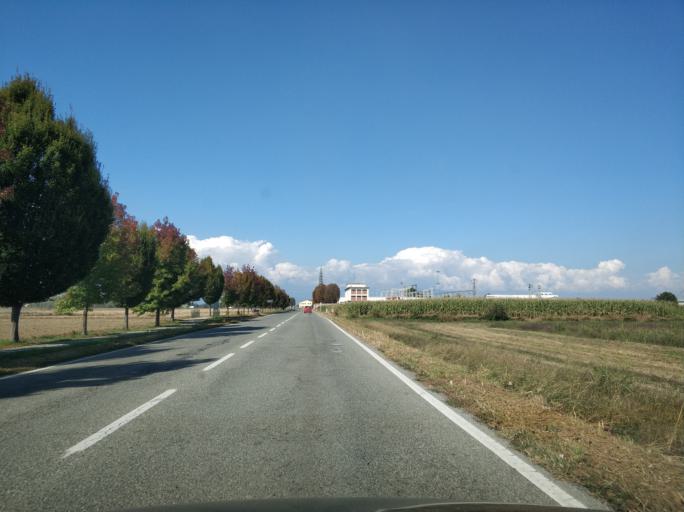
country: IT
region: Piedmont
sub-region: Provincia di Torino
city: Borgaro Torinese
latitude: 45.1480
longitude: 7.6771
